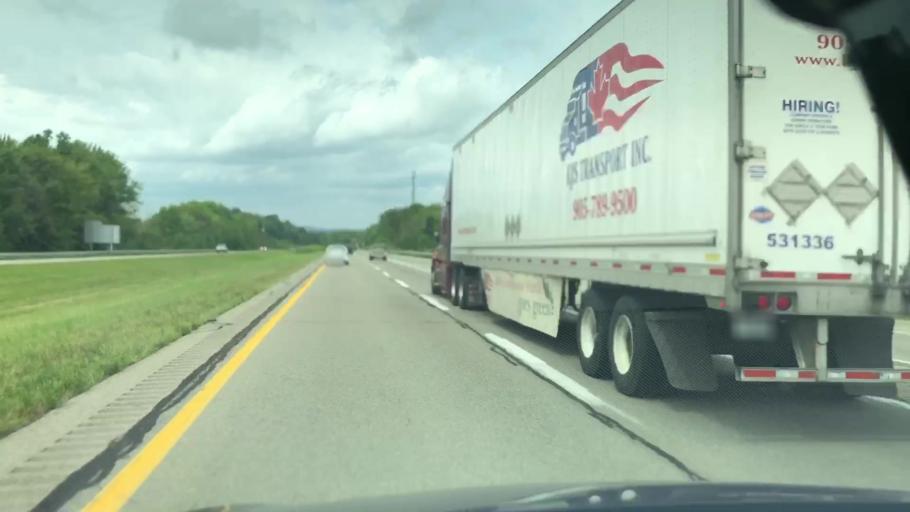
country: US
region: Pennsylvania
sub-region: Crawford County
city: Meadville
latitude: 41.7184
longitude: -80.2016
